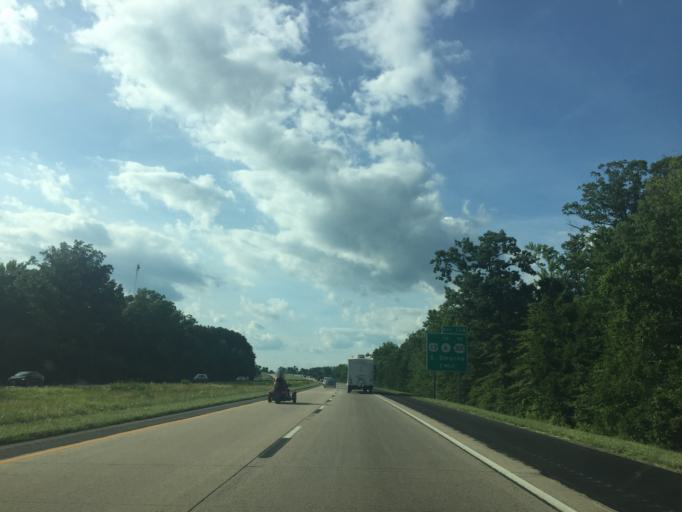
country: US
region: Delaware
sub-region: Kent County
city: Smyrna
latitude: 39.2644
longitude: -75.5789
